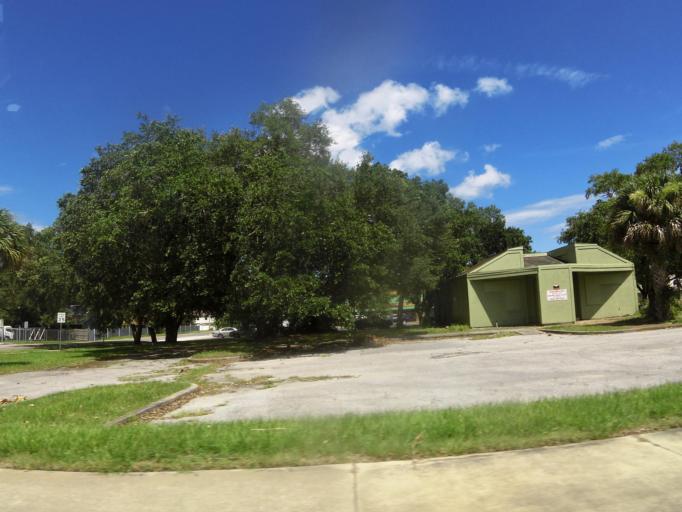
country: US
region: Florida
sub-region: Nassau County
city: Fernandina Beach
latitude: 30.6570
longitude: -81.4533
